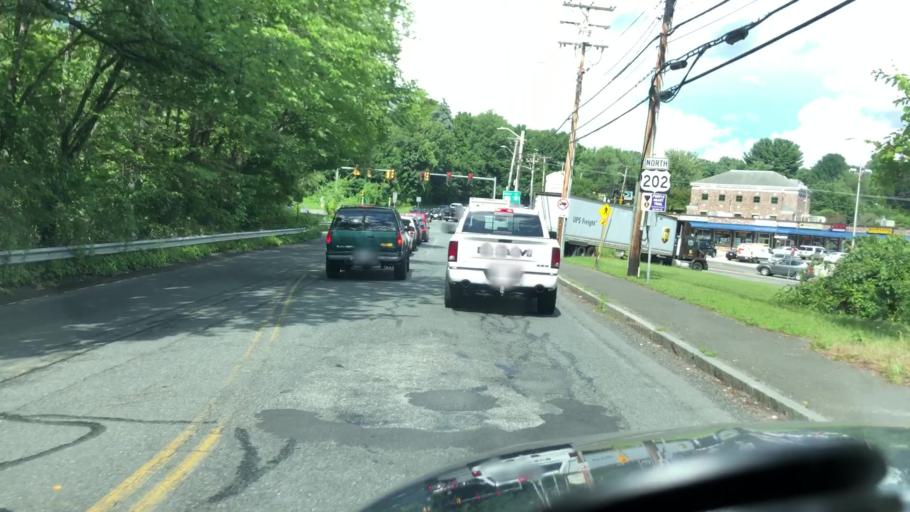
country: US
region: Massachusetts
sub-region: Hampden County
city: Holyoke
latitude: 42.1865
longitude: -72.6516
